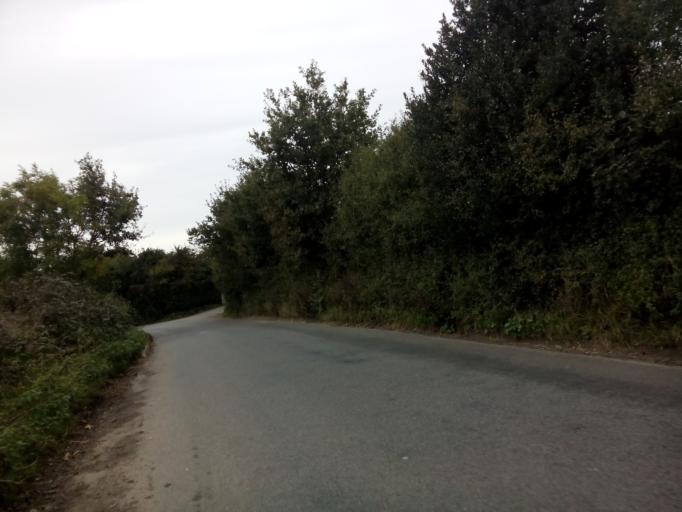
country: GB
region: England
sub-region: Suffolk
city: Ipswich
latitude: 52.0136
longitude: 1.1284
